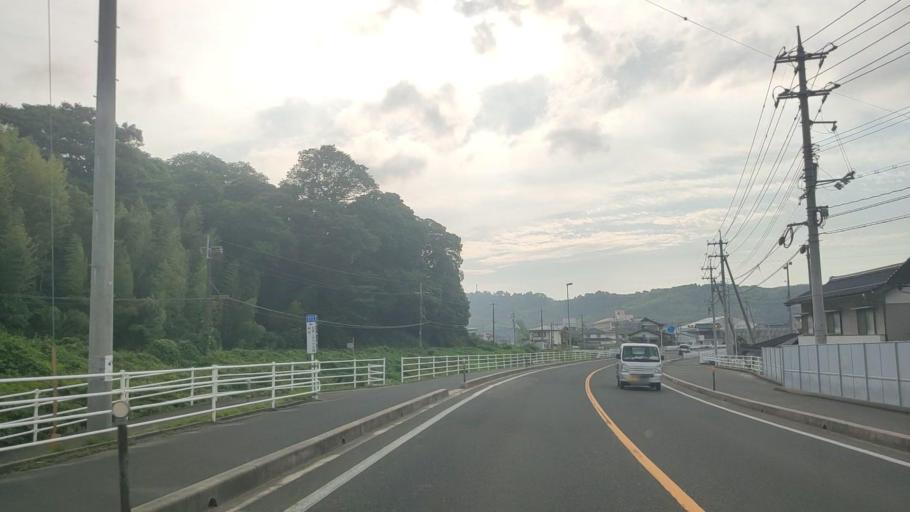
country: JP
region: Tottori
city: Kurayoshi
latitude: 35.4583
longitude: 133.8379
